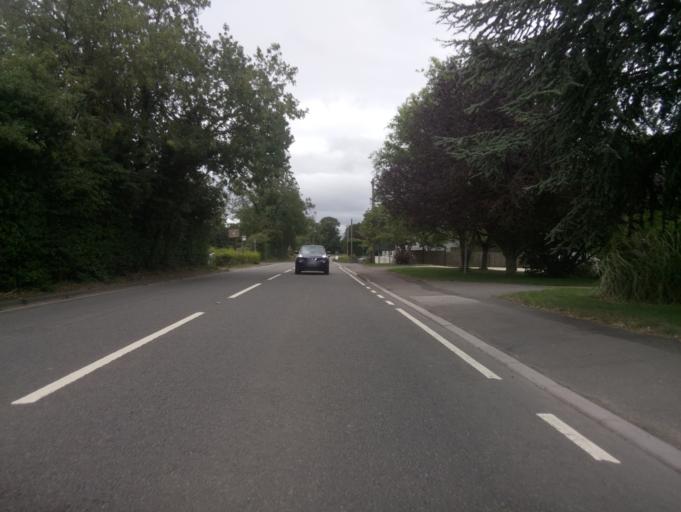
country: GB
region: England
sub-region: Gloucestershire
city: Tewkesbury
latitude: 52.0181
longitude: -2.1654
